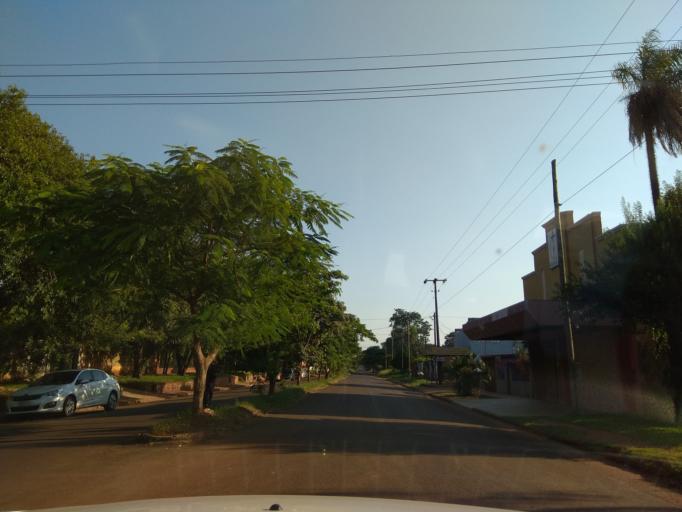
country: AR
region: Misiones
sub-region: Departamento de Capital
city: Posadas
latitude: -27.3696
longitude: -55.9283
